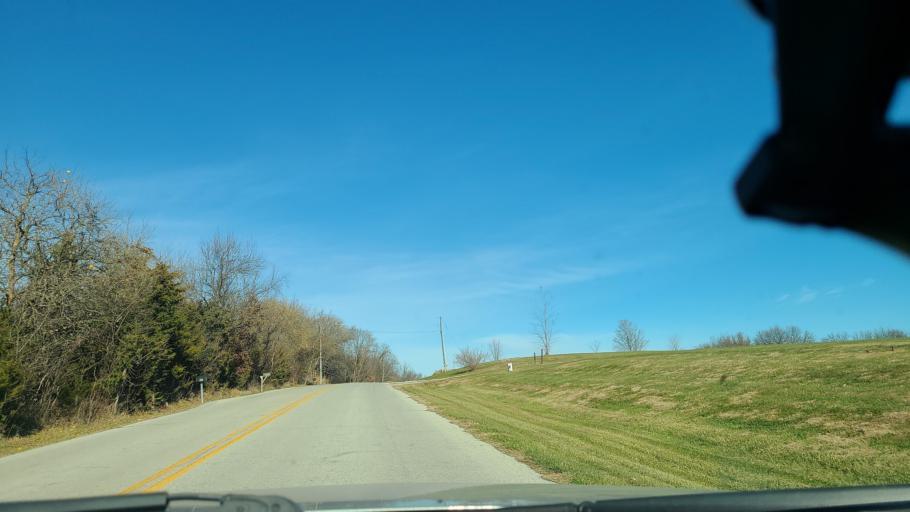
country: US
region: Kansas
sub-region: Leavenworth County
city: Lansing
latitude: 39.1965
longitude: -94.8639
